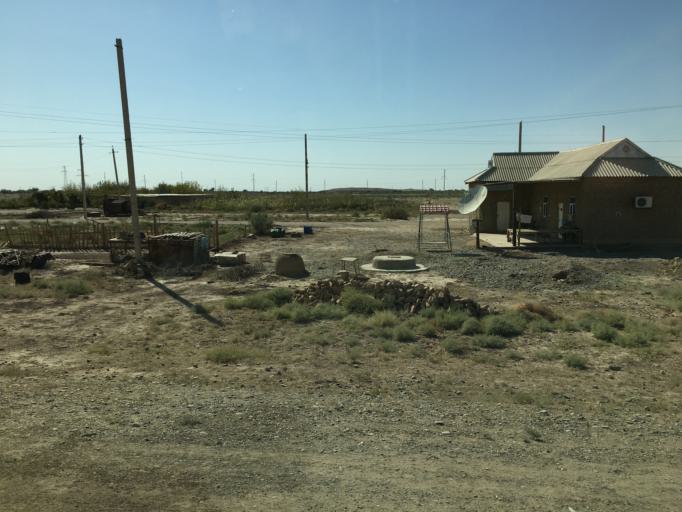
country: IR
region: Razavi Khorasan
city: Sarakhs
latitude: 36.5197
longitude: 61.2506
